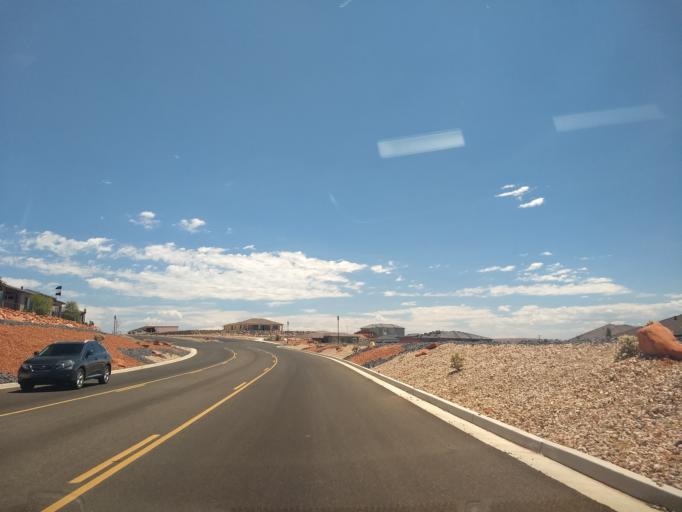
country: US
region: Utah
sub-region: Washington County
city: Washington
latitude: 37.1594
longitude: -113.5275
